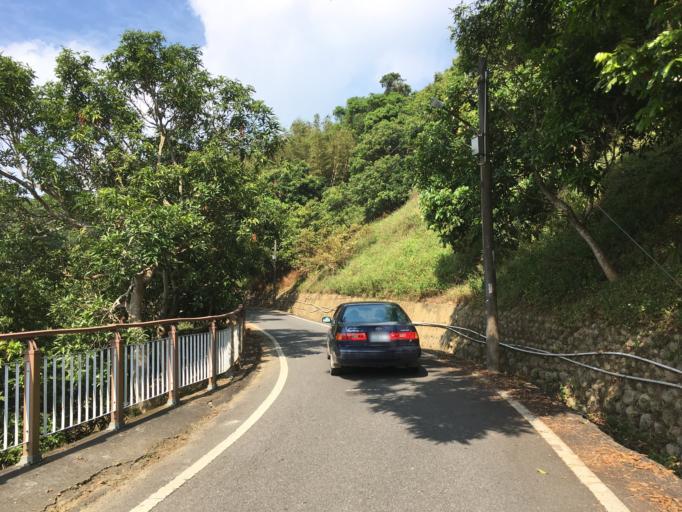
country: TW
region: Taiwan
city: Fengyuan
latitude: 24.1803
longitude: 120.7841
